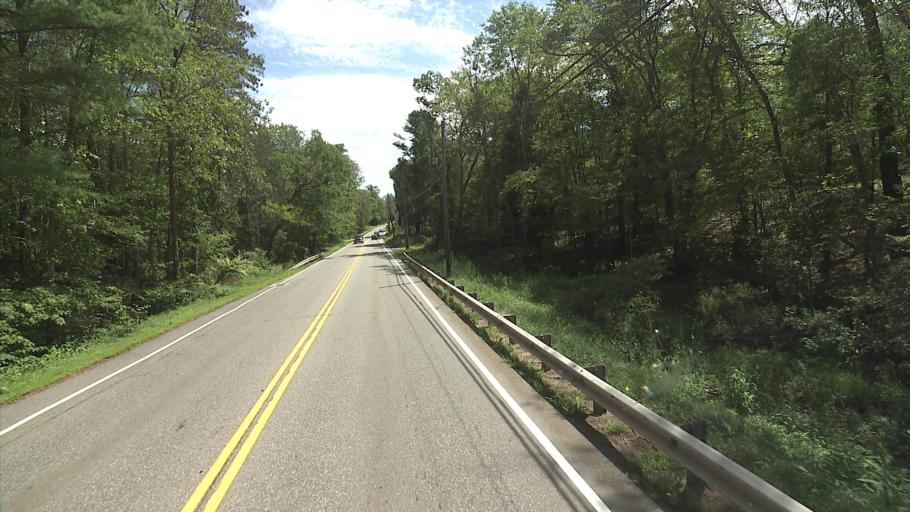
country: US
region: Connecticut
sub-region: Tolland County
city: Mansfield City
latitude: 41.7693
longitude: -72.2018
